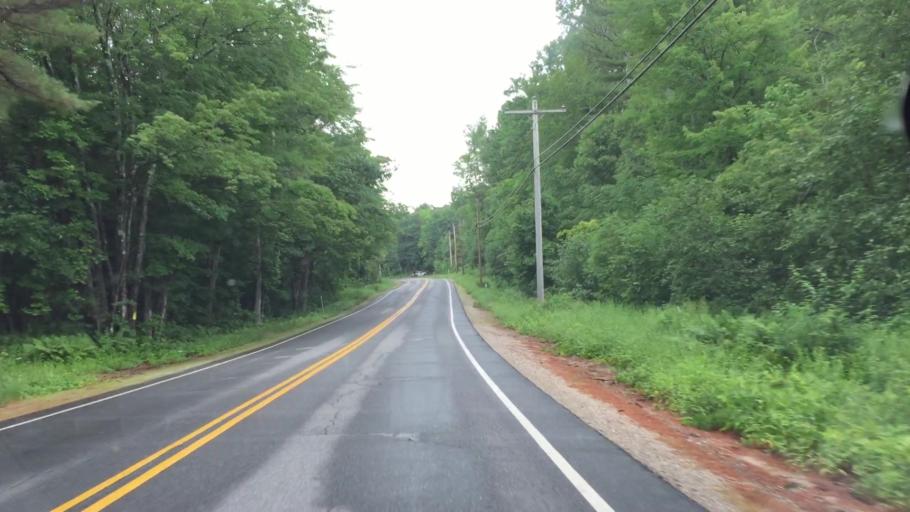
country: US
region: New Hampshire
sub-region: Carroll County
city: Center Harbor
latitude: 43.7444
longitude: -71.4781
